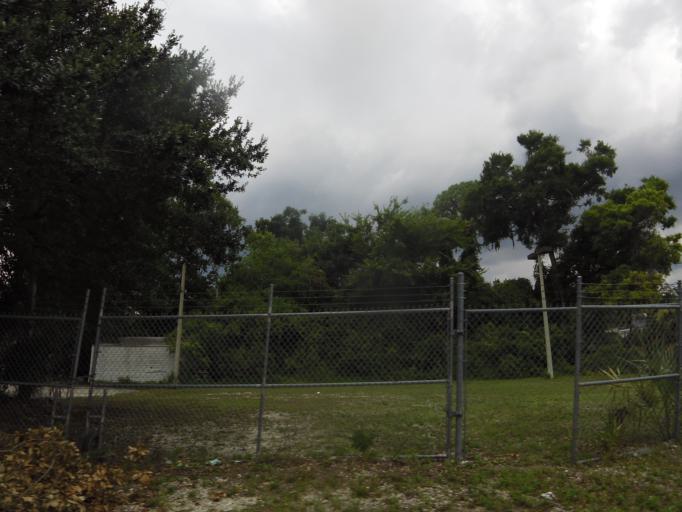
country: US
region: Florida
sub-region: Duval County
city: Jacksonville
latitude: 30.3240
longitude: -81.5359
